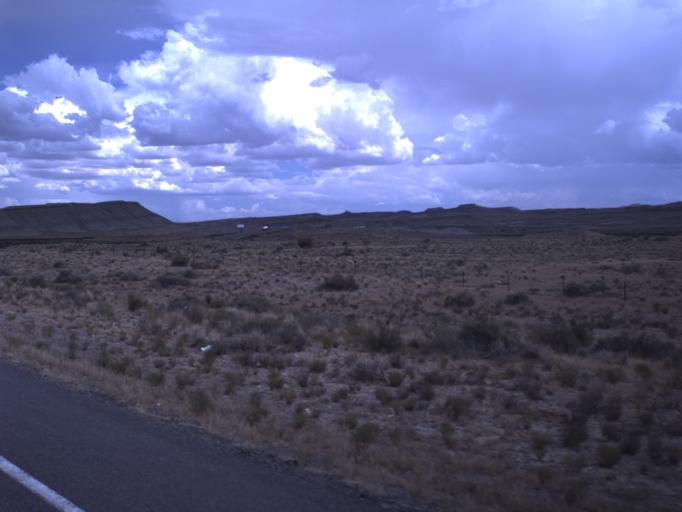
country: US
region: Utah
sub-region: Carbon County
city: East Carbon City
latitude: 38.9909
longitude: -110.1315
